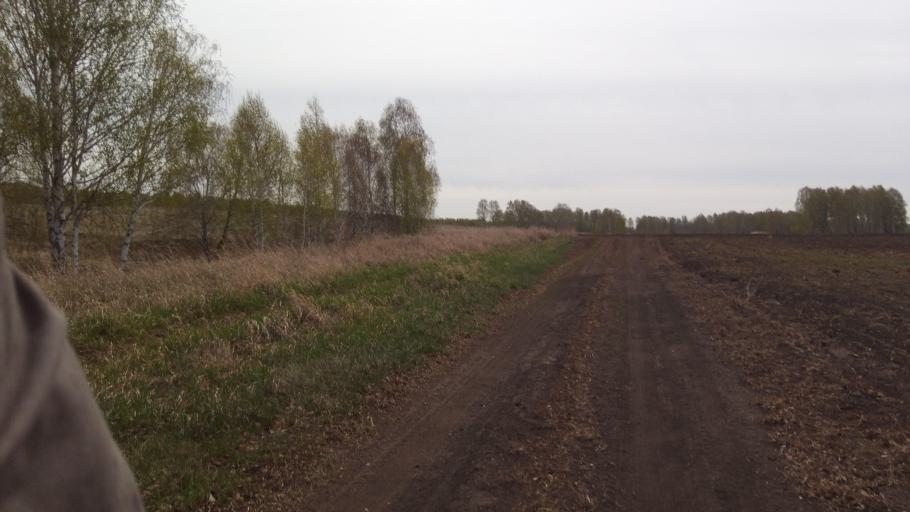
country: RU
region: Chelyabinsk
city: Timiryazevskiy
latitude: 55.0157
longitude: 60.8576
